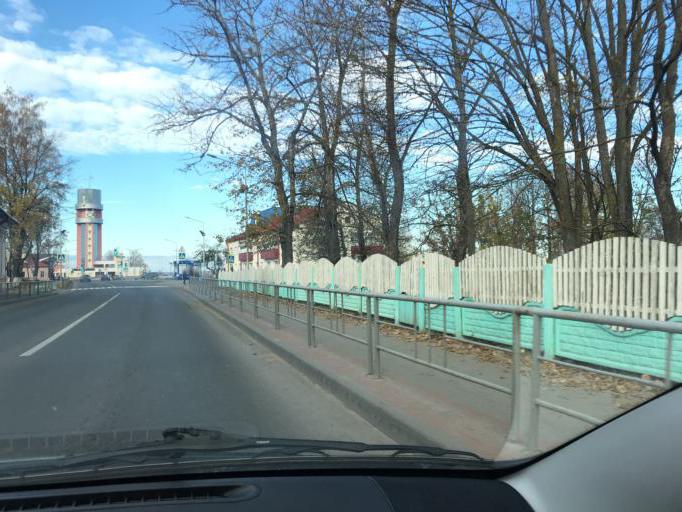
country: BY
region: Vitebsk
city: Haradok
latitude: 55.4628
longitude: 29.9854
